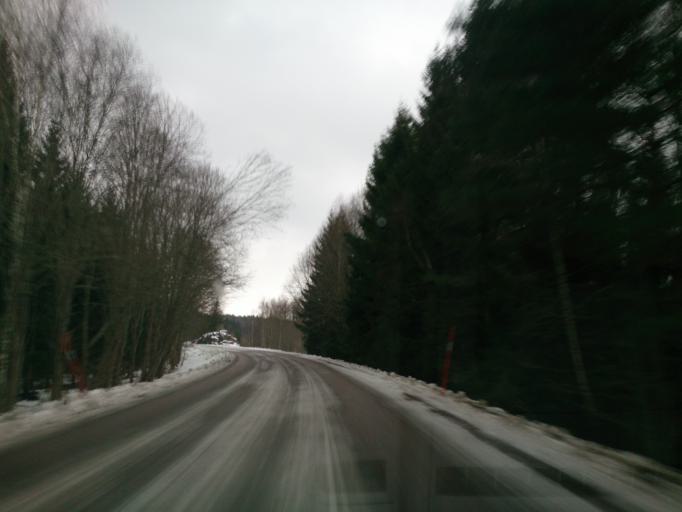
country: SE
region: OEstergoetland
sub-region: Atvidabergs Kommun
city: Atvidaberg
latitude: 58.2352
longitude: 16.0086
